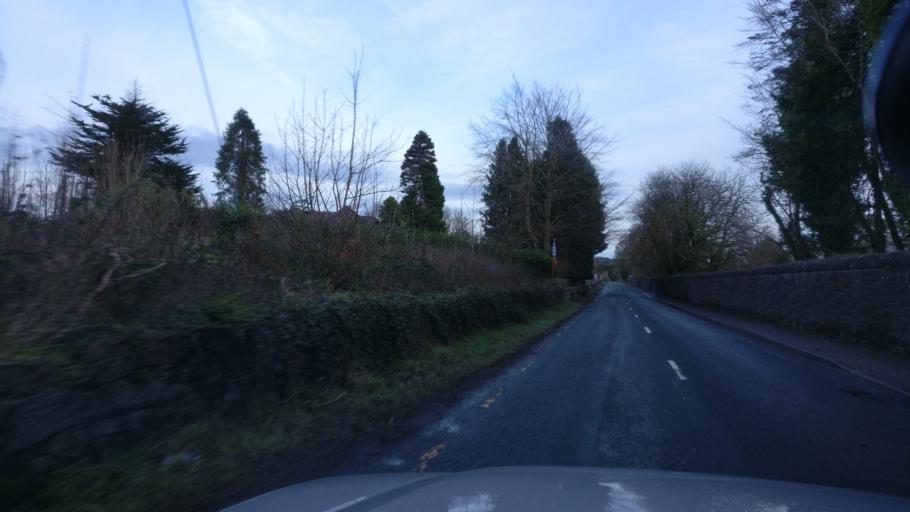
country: IE
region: Connaught
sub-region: Maigh Eo
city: Ballinrobe
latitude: 53.5424
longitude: -9.2732
